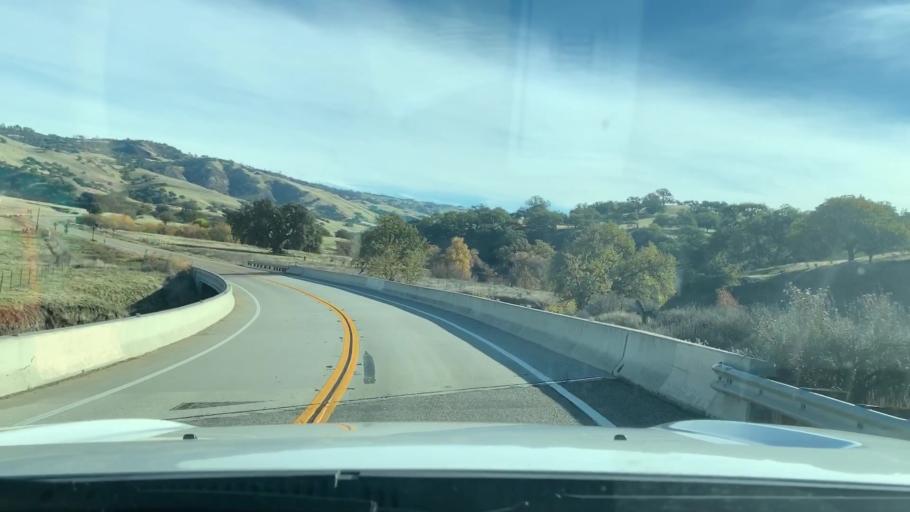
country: US
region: California
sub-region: Monterey County
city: King City
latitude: 36.1857
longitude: -120.8255
